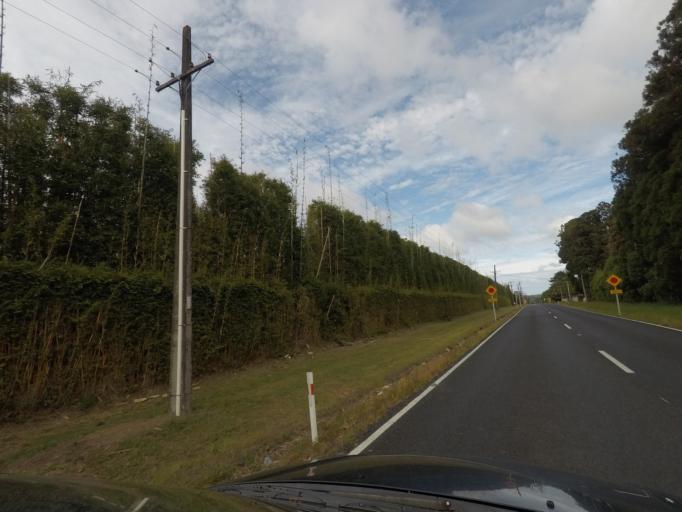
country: NZ
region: Auckland
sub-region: Auckland
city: Rosebank
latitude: -36.7761
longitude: 174.5792
